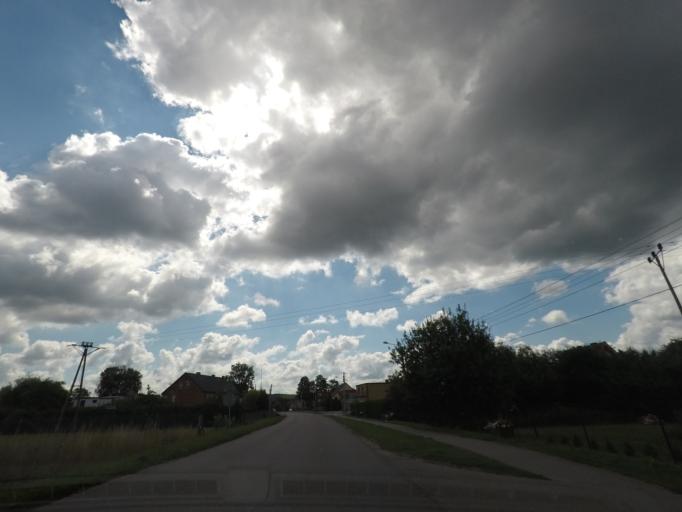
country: PL
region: Pomeranian Voivodeship
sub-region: Powiat wejherowski
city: Leczyce
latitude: 54.5861
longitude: 17.8620
